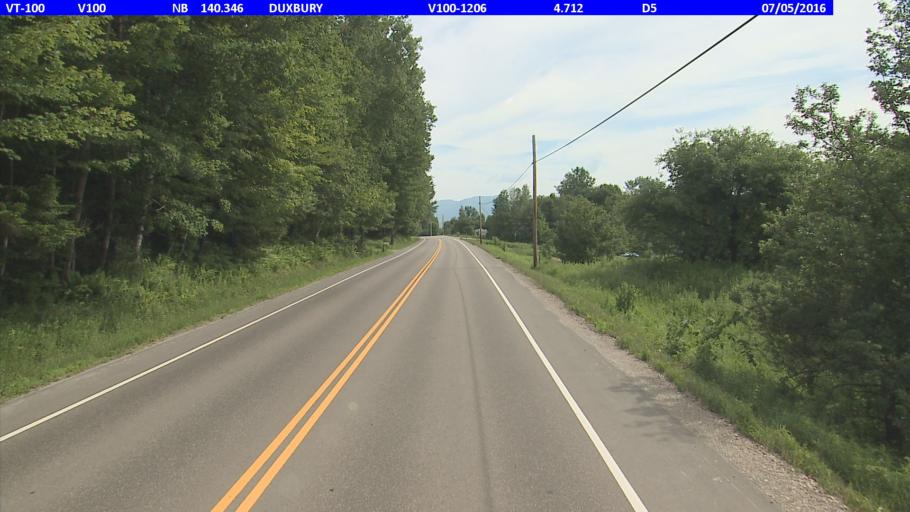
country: US
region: Vermont
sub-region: Washington County
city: Waterbury
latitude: 44.3108
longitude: -72.7661
